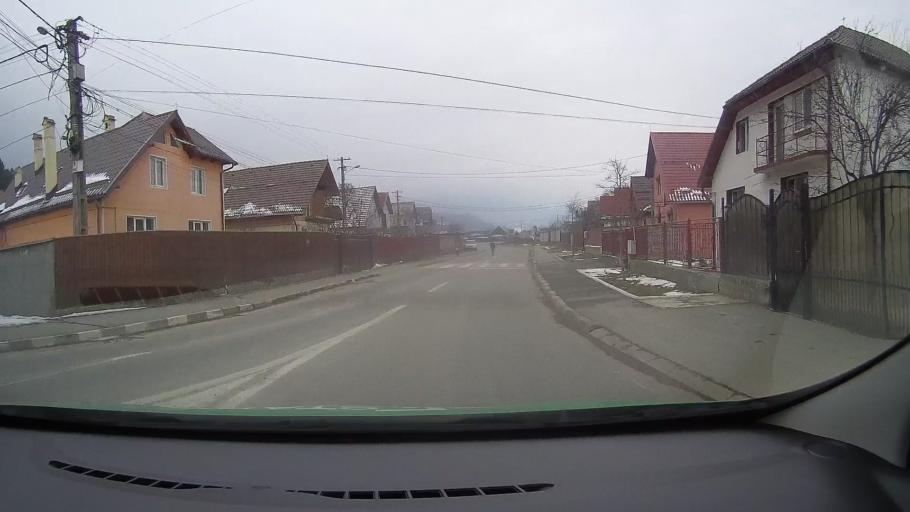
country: RO
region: Brasov
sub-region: Oras Rasnov
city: Rasnov
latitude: 45.5774
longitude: 25.4568
